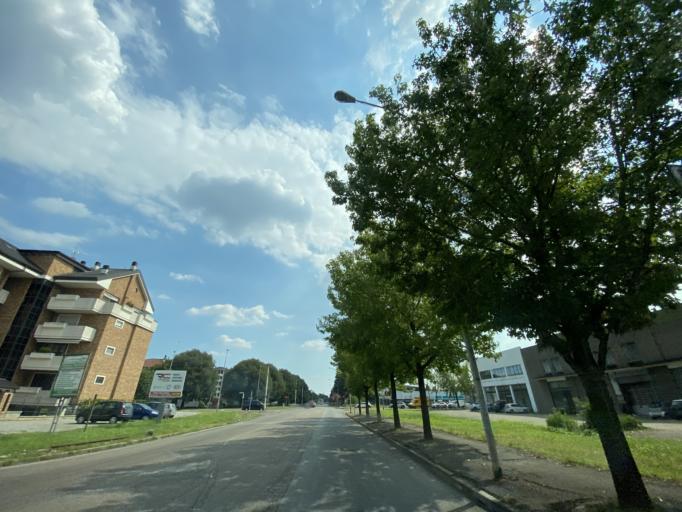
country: IT
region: Lombardy
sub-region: Provincia di Monza e Brianza
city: Nova Milanese
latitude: 45.5980
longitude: 9.1998
